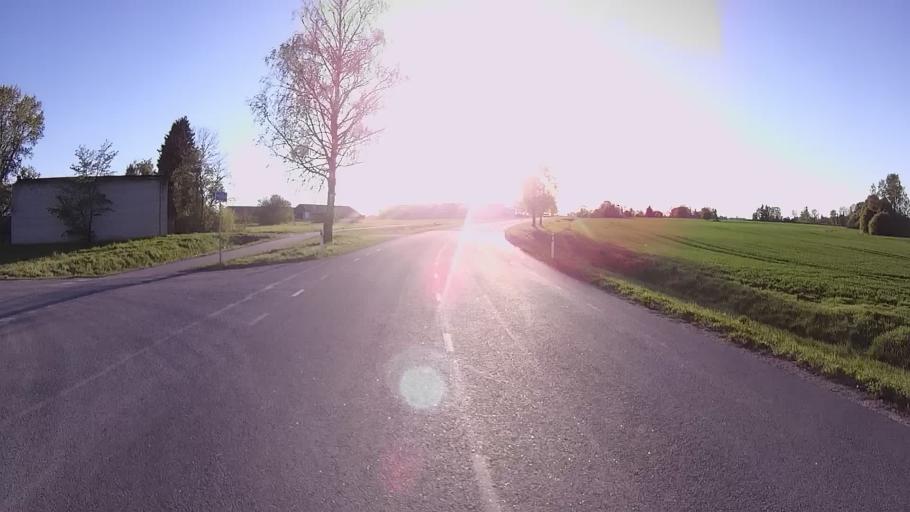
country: EE
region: Jogevamaa
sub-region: Poltsamaa linn
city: Poltsamaa
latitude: 58.5344
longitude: 25.9329
